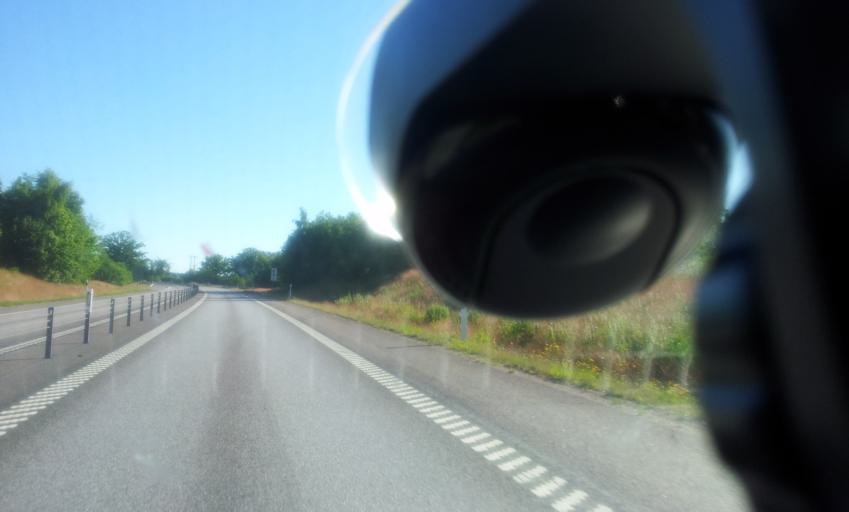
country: SE
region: Kalmar
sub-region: Kalmar Kommun
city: Ljungbyholm
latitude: 56.5792
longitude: 16.1132
